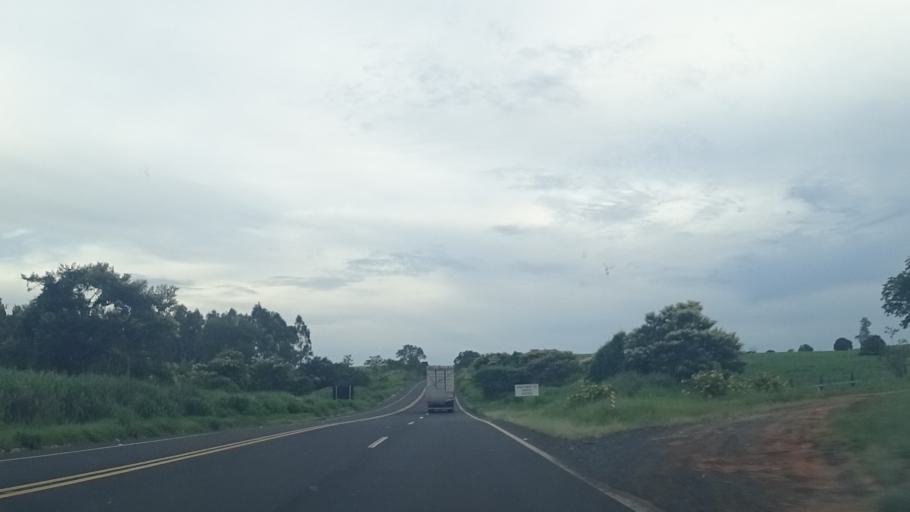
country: BR
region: Sao Paulo
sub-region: Martinopolis
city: Martinopolis
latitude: -22.1147
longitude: -51.1644
